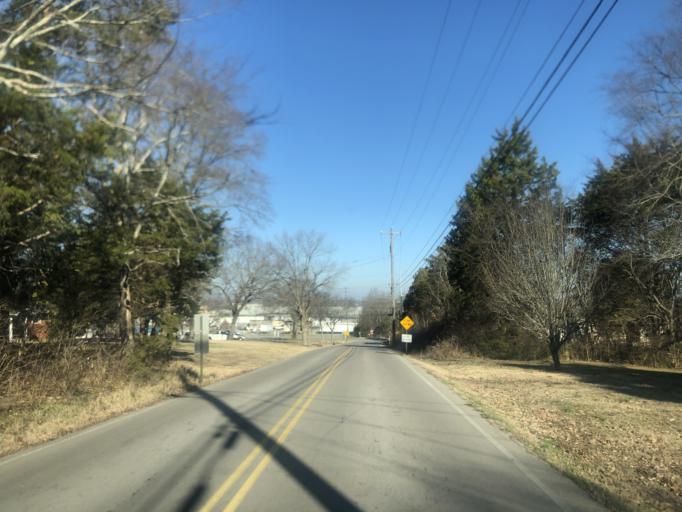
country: US
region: Tennessee
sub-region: Rutherford County
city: La Vergne
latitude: 36.0146
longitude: -86.5819
